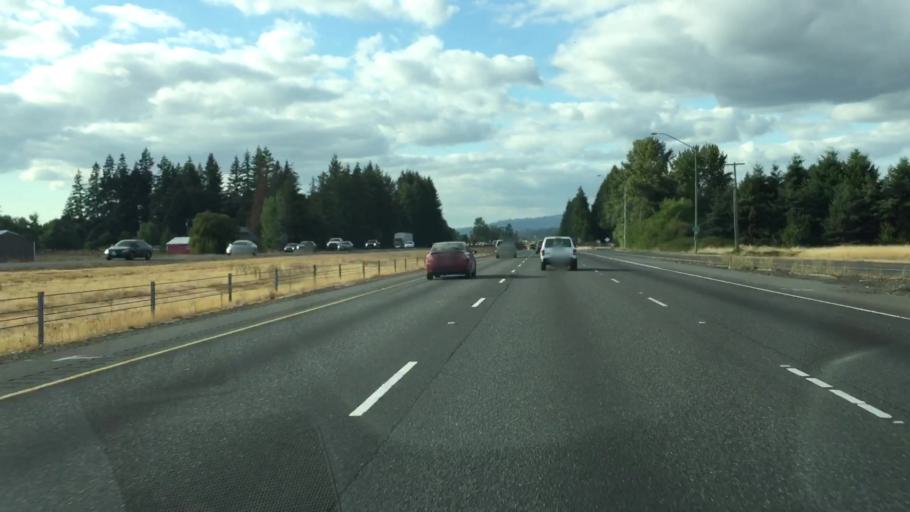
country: US
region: Washington
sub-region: Clark County
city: La Center
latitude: 45.8353
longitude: -122.6948
